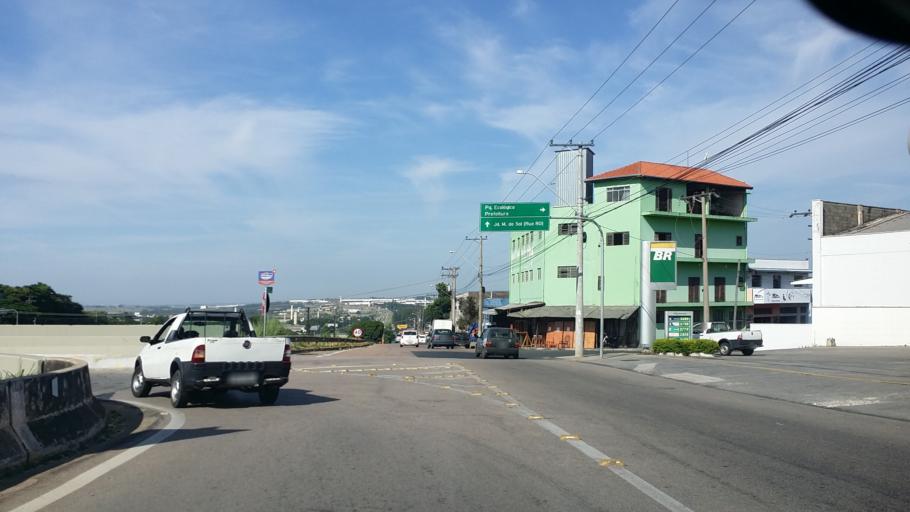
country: BR
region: Sao Paulo
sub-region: Indaiatuba
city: Indaiatuba
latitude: -23.1240
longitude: -47.2261
